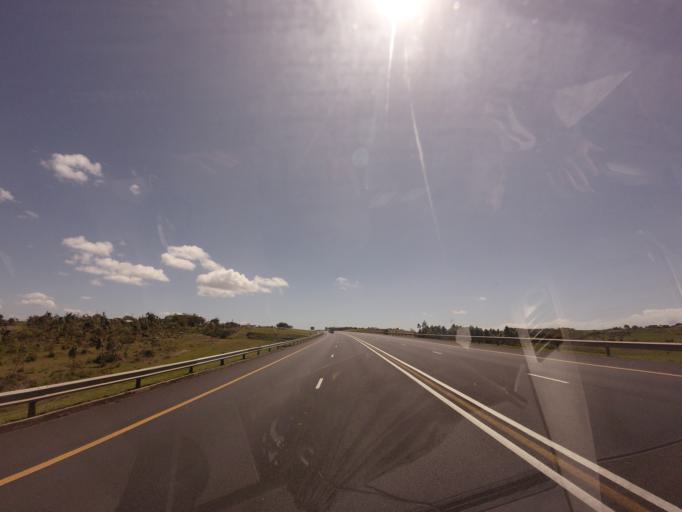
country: ZA
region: KwaZulu-Natal
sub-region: iLembe District Municipality
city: Mandeni
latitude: -29.0932
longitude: 31.6007
